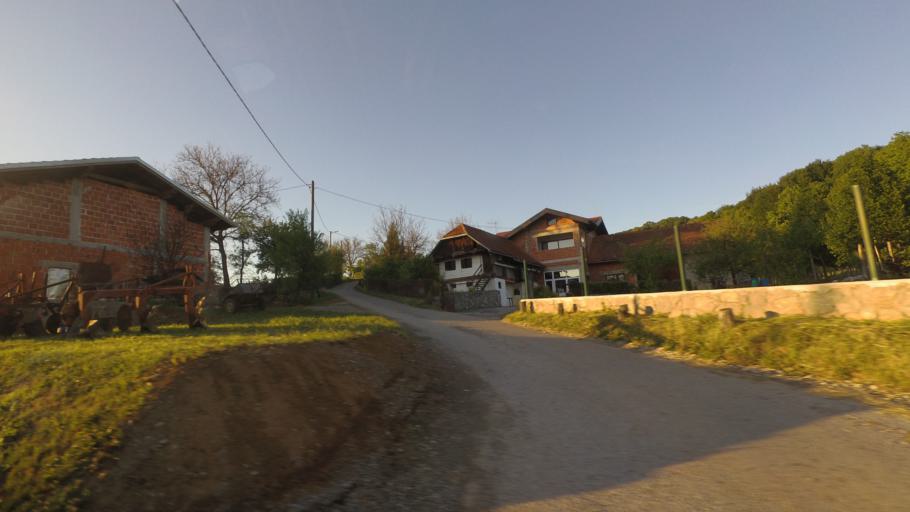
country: HR
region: Karlovacka
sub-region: Grad Karlovac
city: Karlovac
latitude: 45.4148
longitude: 15.5556
